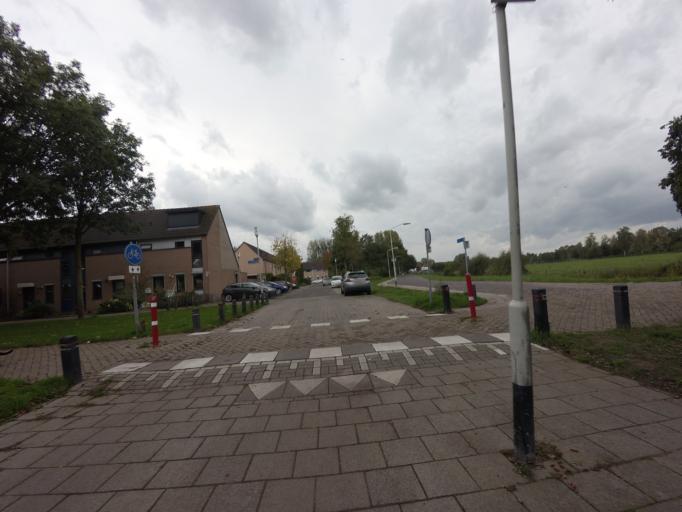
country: NL
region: North Brabant
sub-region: Gemeente Breda
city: Hoge Vucht
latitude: 51.6258
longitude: 4.7492
